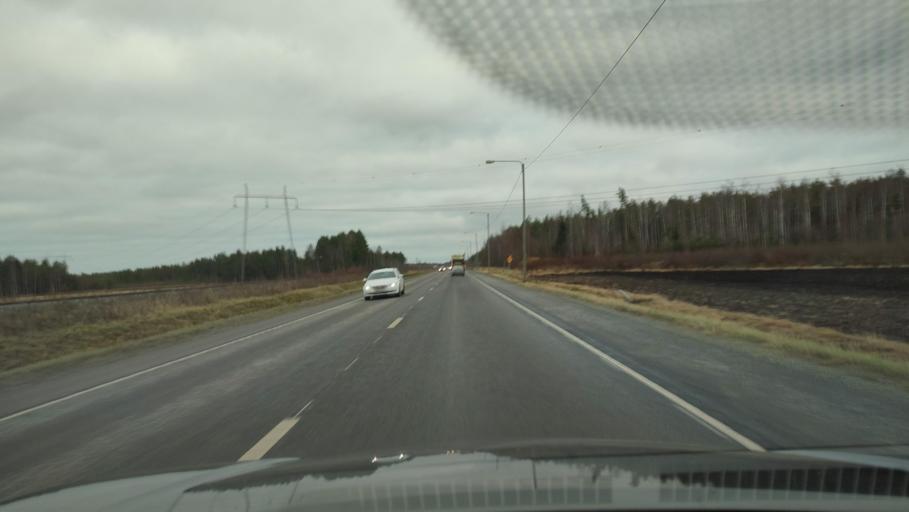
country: FI
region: Southern Ostrobothnia
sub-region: Seinaejoki
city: Ilmajoki
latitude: 62.7455
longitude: 22.6323
